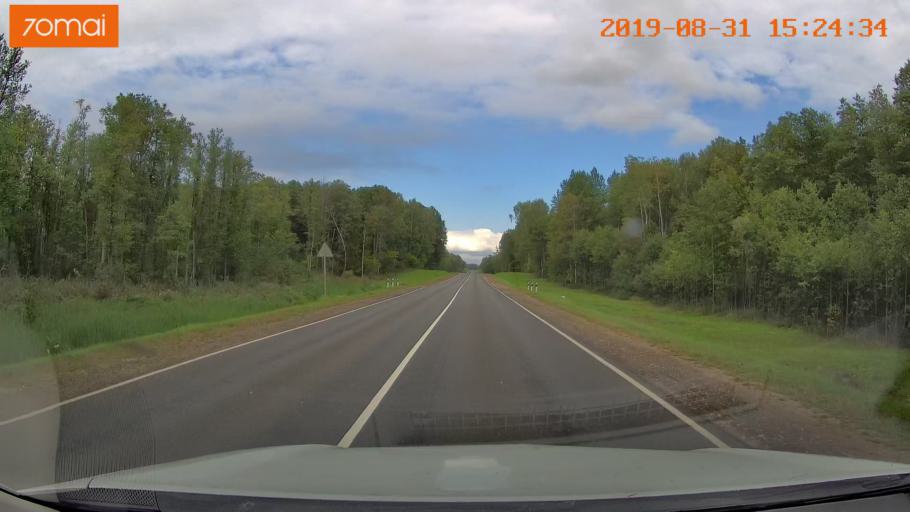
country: RU
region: Kaluga
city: Baryatino
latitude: 54.5294
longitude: 34.5065
